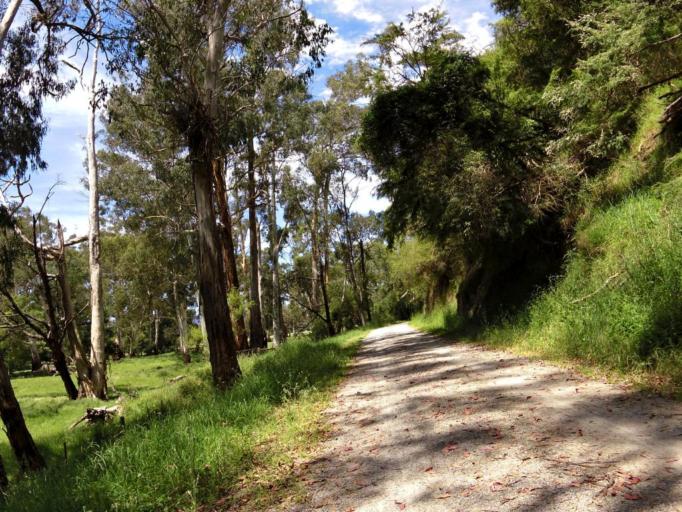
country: AU
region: Victoria
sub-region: Yarra Ranges
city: Launching Place
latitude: -37.7681
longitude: 145.5539
